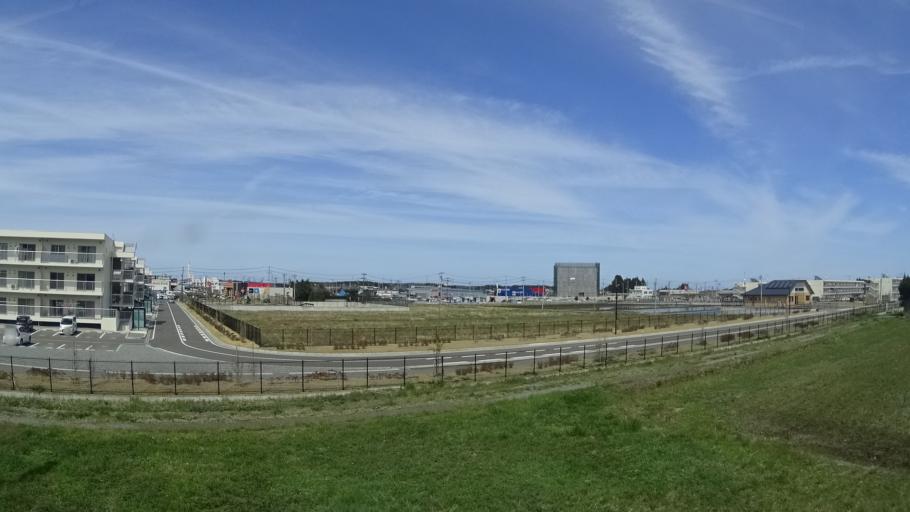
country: JP
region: Fukushima
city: Namie
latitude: 37.6250
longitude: 140.9861
